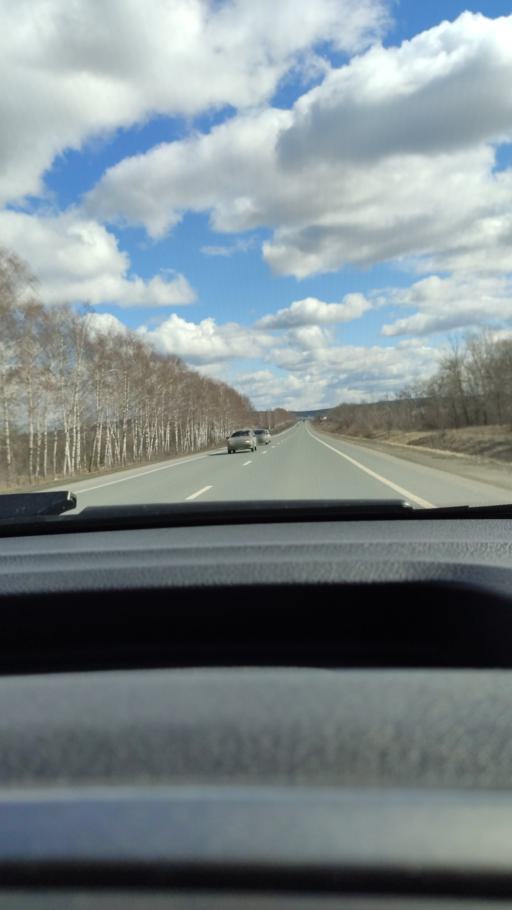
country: RU
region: Samara
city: Kurumoch
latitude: 53.4880
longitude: 49.9992
